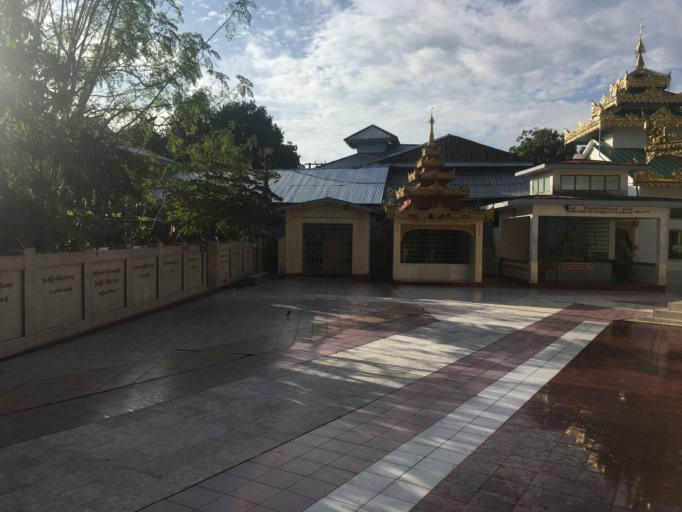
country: MM
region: Mon
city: Mawlamyine
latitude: 16.4791
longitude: 97.6225
